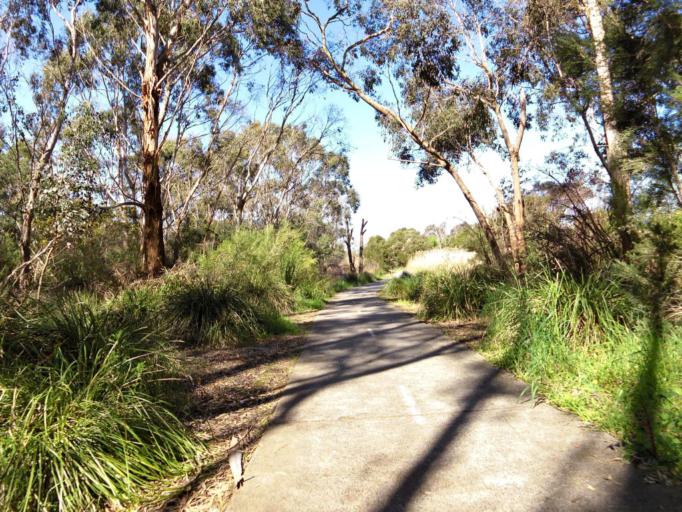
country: AU
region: Victoria
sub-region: Monash
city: Mulgrave
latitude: -37.9232
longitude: 145.2051
